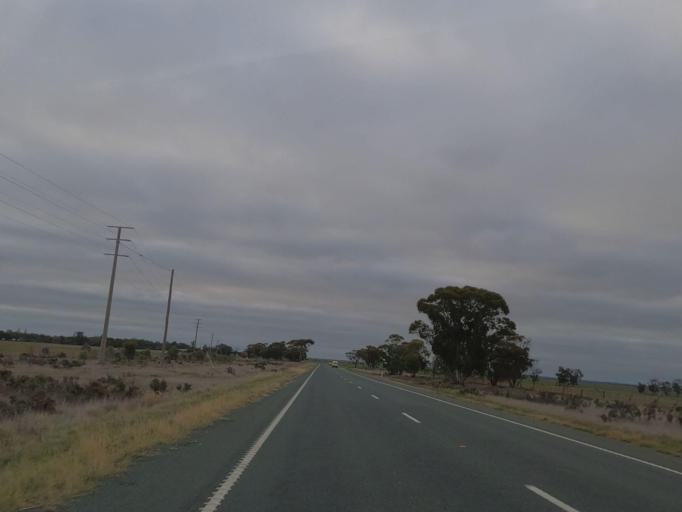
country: AU
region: Victoria
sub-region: Swan Hill
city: Swan Hill
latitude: -35.5664
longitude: 143.7841
